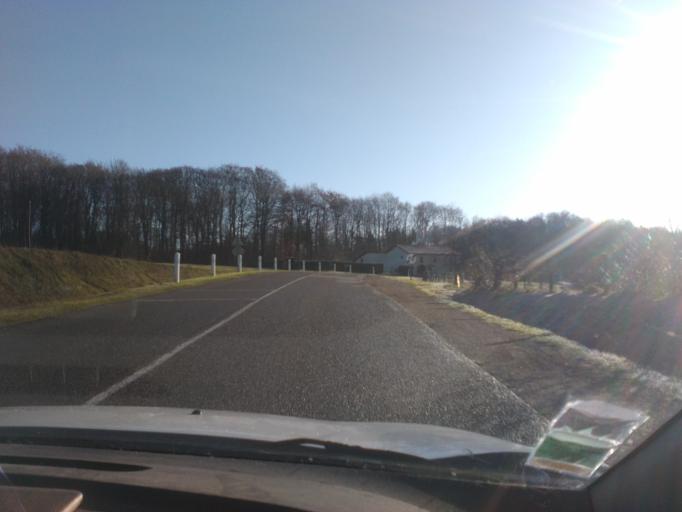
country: FR
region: Lorraine
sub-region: Departement des Vosges
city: Xertigny
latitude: 48.0347
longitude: 6.4167
